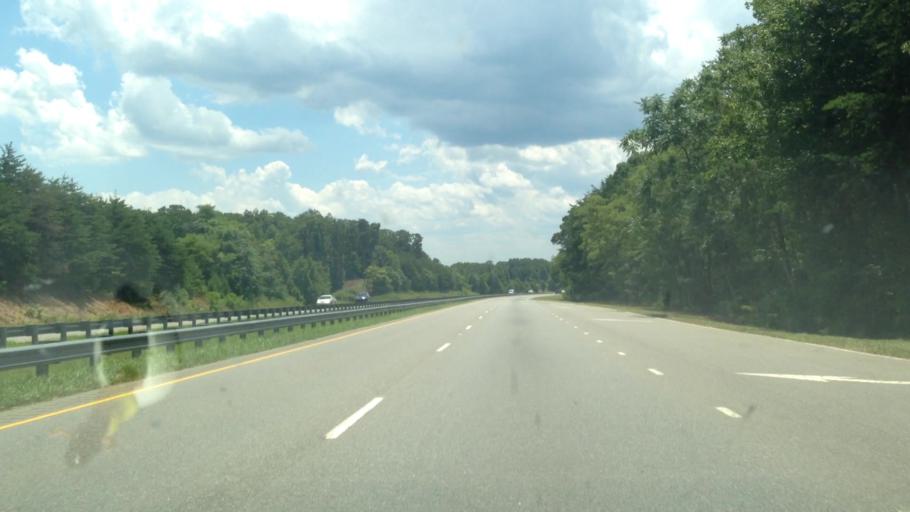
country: US
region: North Carolina
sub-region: Rockingham County
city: Stoneville
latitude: 36.4994
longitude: -79.9223
